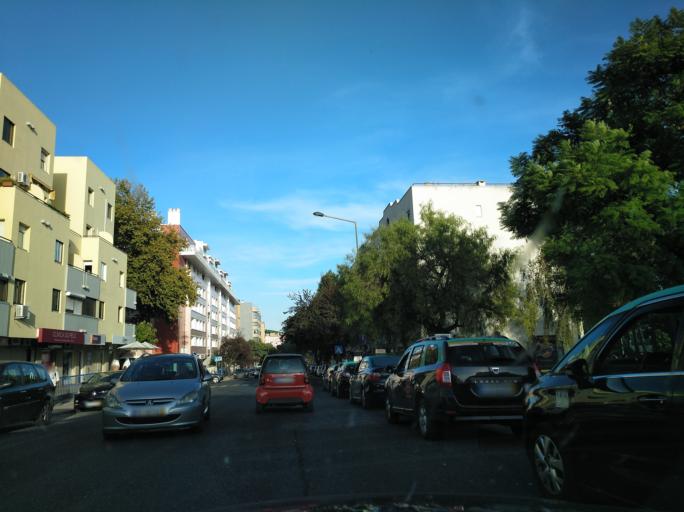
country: PT
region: Lisbon
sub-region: Odivelas
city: Olival do Basto
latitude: 38.7605
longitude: -9.1688
